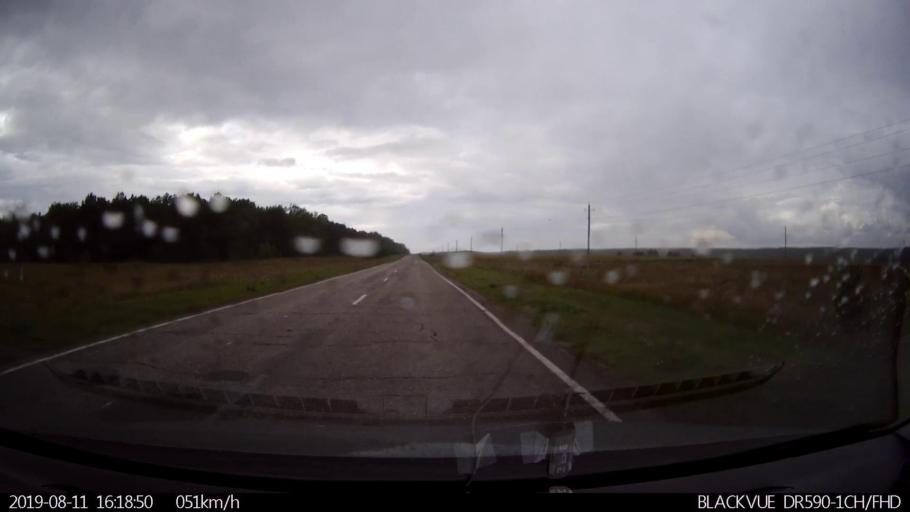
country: RU
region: Ulyanovsk
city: Mayna
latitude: 54.0581
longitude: 47.6104
